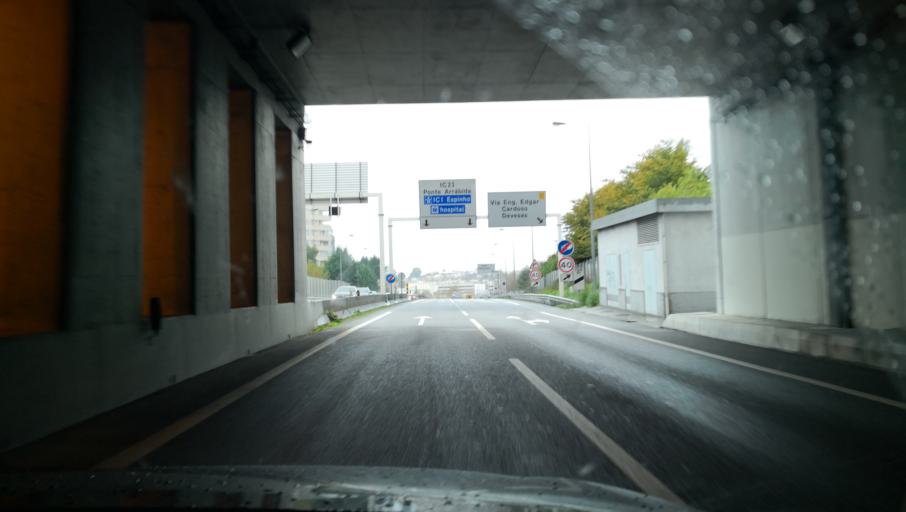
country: PT
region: Porto
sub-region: Vila Nova de Gaia
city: Vila Nova de Gaia
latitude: 41.1228
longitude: -8.6145
